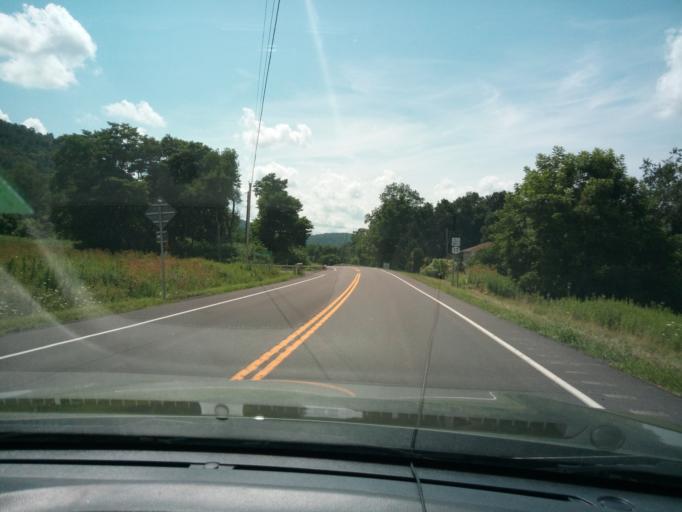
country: US
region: Pennsylvania
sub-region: Bradford County
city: South Waverly
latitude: 42.0213
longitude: -76.6760
